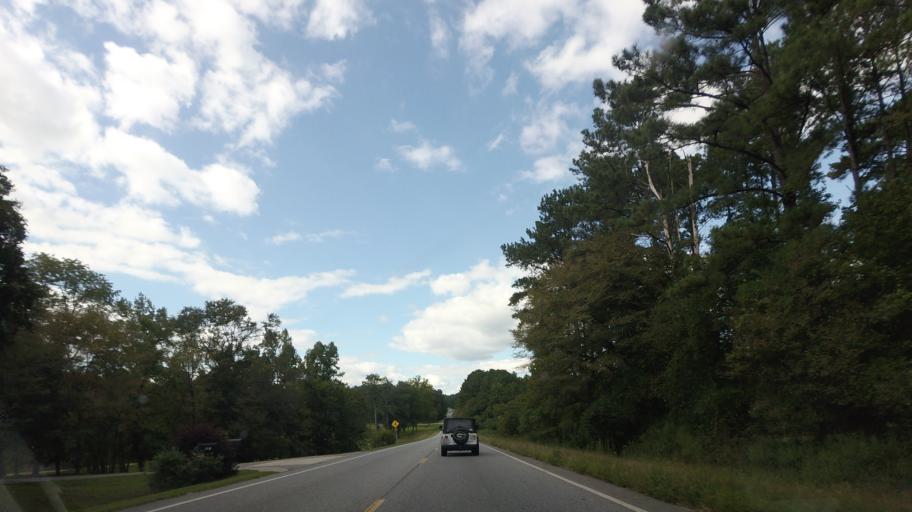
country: US
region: Georgia
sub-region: Bibb County
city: Macon
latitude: 32.9556
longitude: -83.7256
